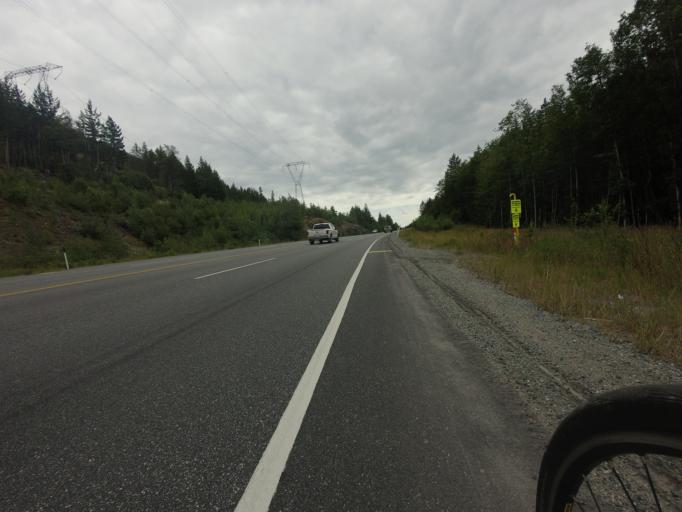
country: CA
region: British Columbia
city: Whistler
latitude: 49.8726
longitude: -123.1601
